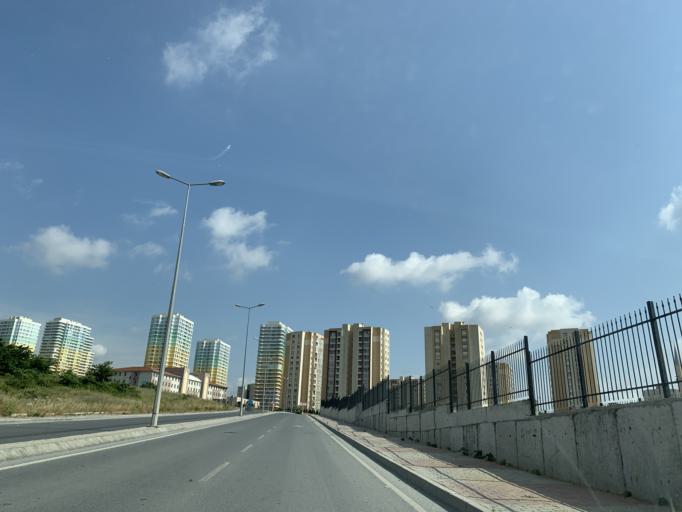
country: TR
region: Istanbul
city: Esenyurt
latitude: 41.0669
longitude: 28.7053
